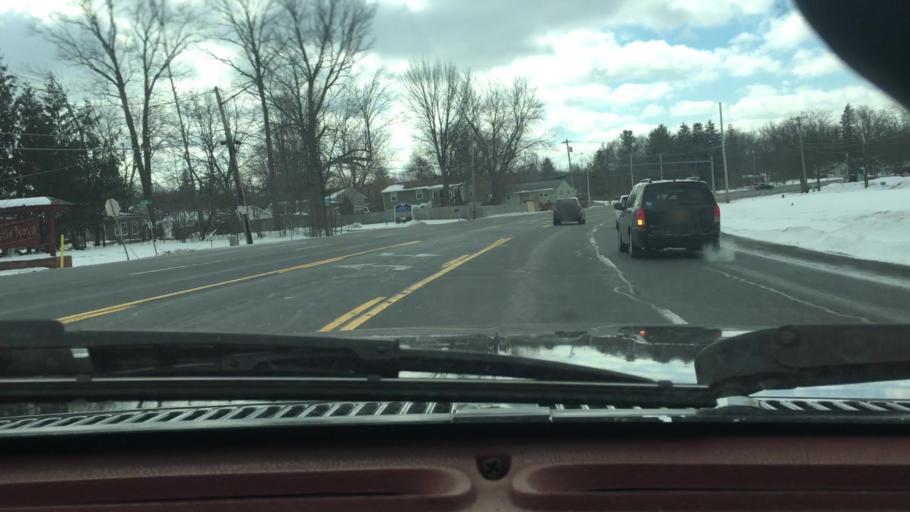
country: US
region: New York
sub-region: Onondaga County
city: Liverpool
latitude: 43.1572
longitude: -76.2277
